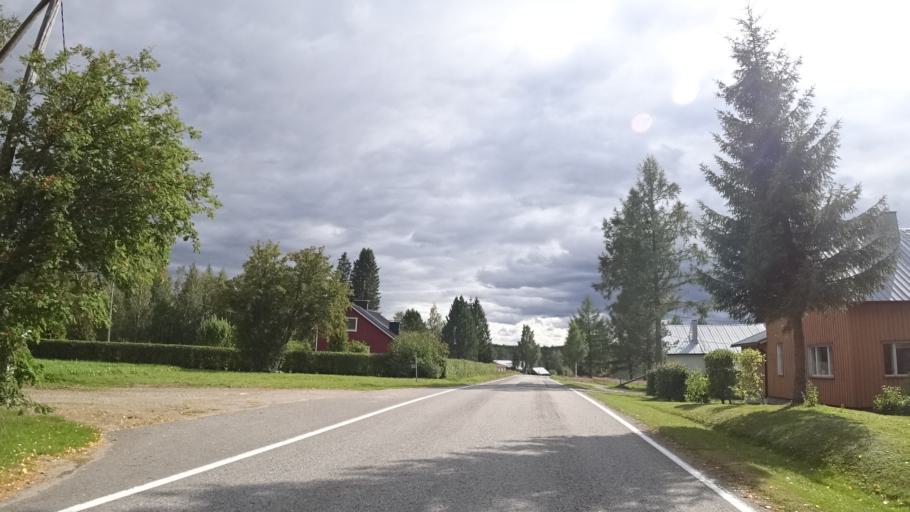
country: FI
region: North Karelia
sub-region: Joensuu
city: Ilomantsi
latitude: 62.4500
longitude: 31.1151
